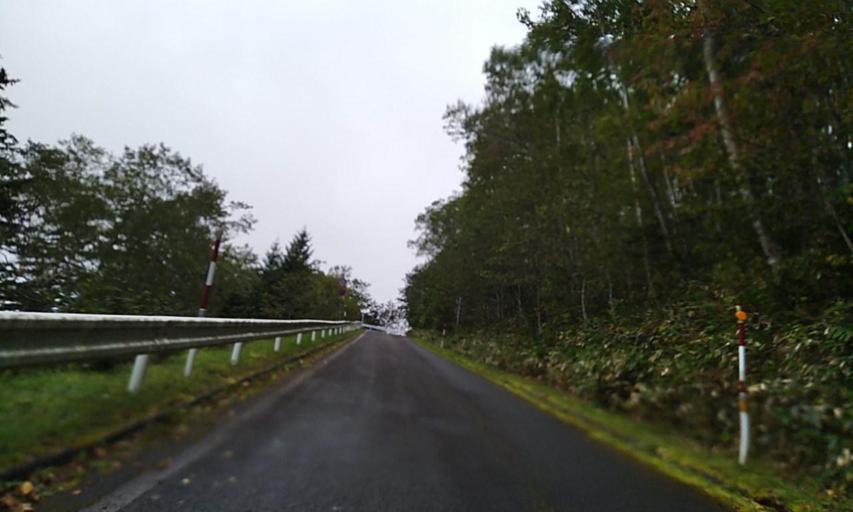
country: JP
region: Hokkaido
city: Bihoro
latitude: 43.5757
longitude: 144.2375
